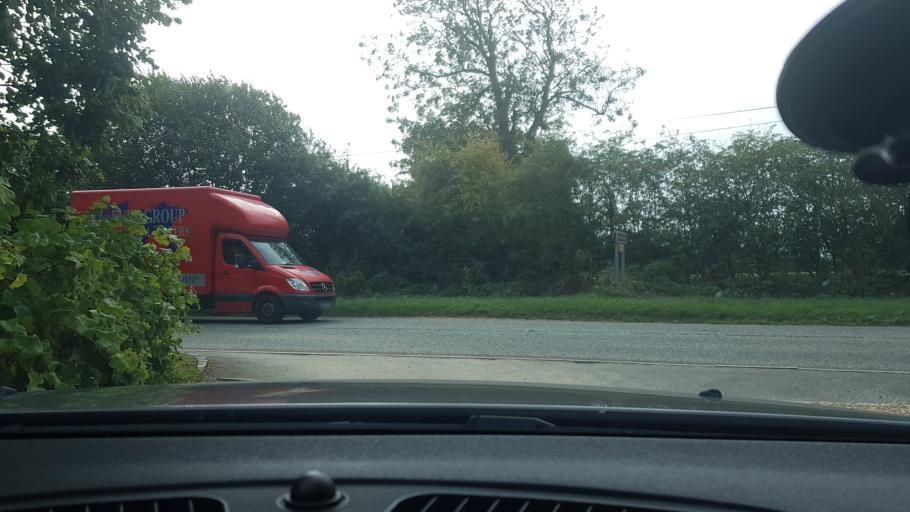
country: GB
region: England
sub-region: West Berkshire
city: Winterbourne
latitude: 51.4126
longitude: -1.3655
